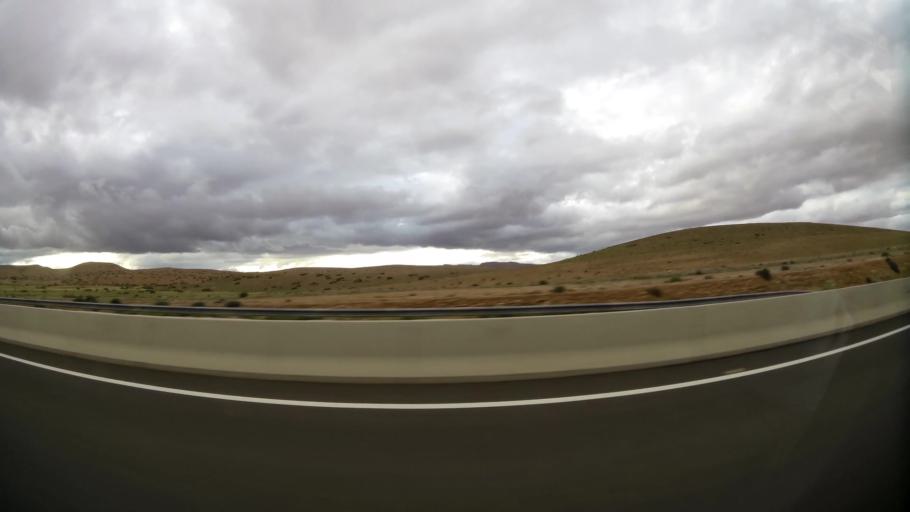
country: MA
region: Taza-Al Hoceima-Taounate
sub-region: Taza
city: Guercif
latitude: 34.3042
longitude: -3.6634
